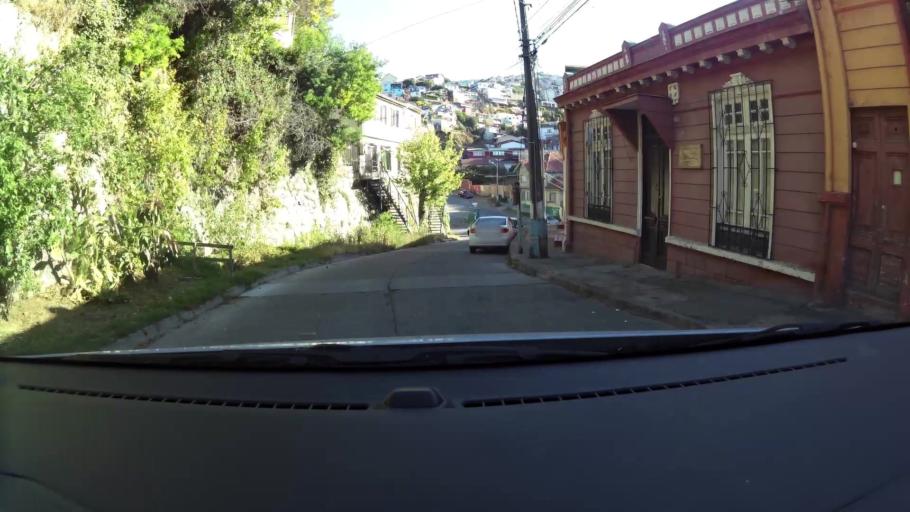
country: CL
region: Valparaiso
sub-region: Provincia de Valparaiso
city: Valparaiso
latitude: -33.0490
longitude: -71.6267
